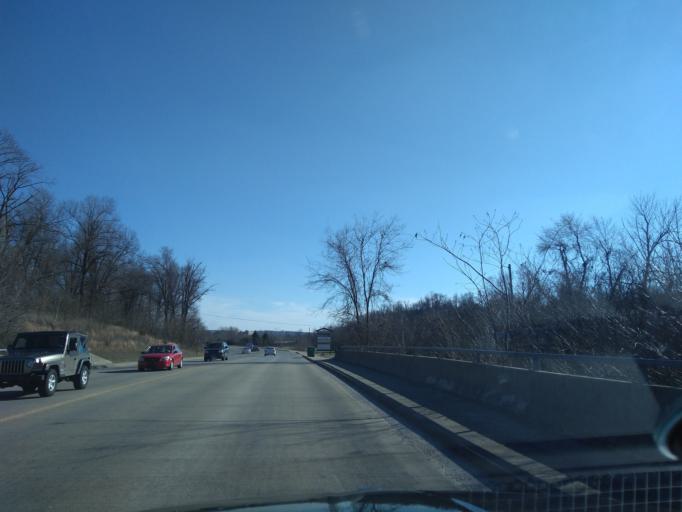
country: US
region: Arkansas
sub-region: Washington County
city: Johnson
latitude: 36.1280
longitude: -94.1631
